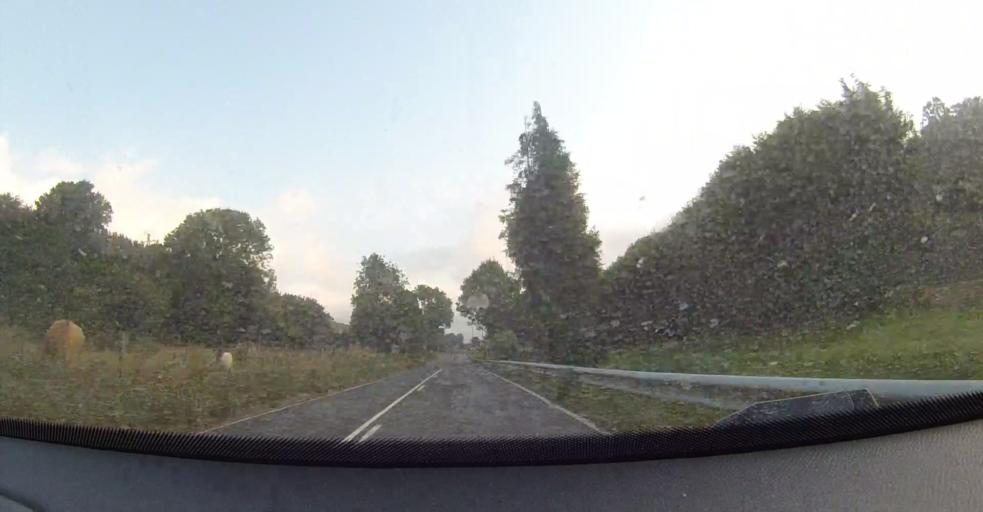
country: ES
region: Basque Country
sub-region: Bizkaia
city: Urrestieta
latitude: 43.2335
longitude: -3.1588
